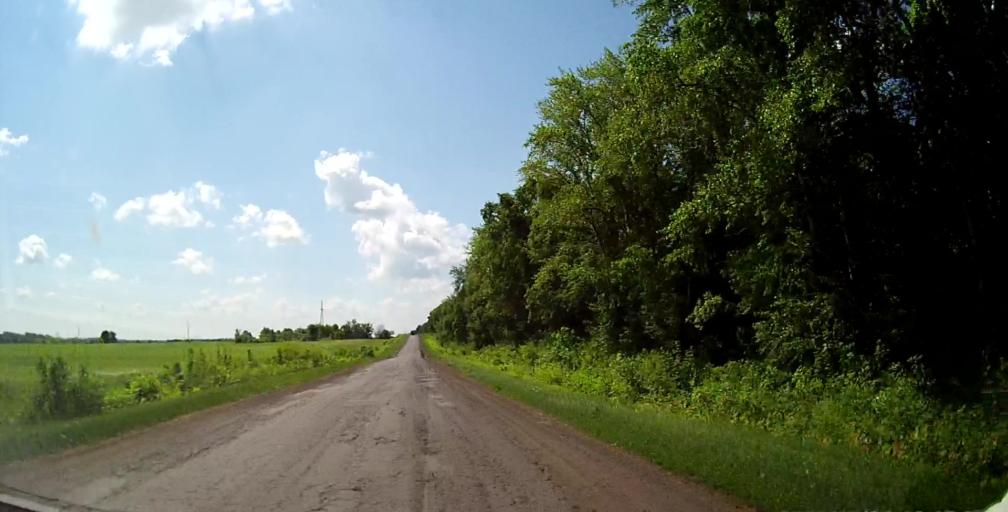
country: RU
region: Lipetsk
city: Chaplygin
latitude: 53.2961
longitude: 39.9554
